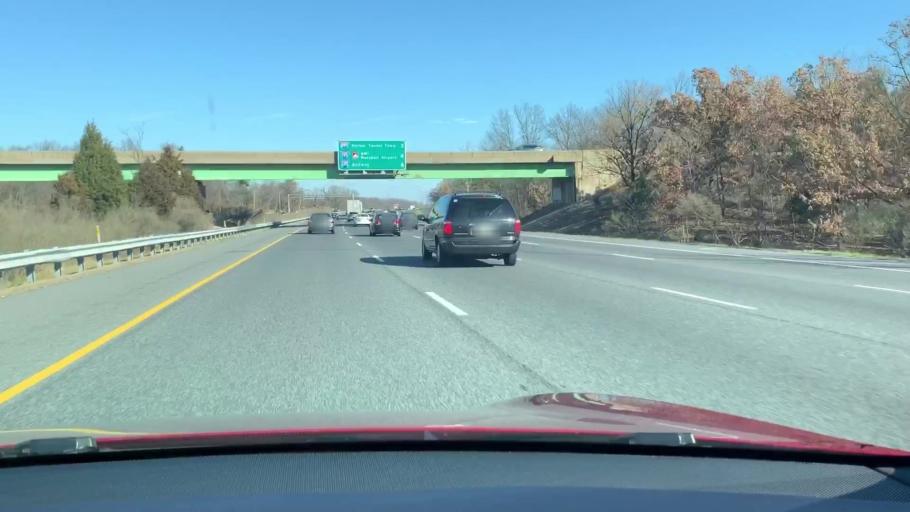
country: US
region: Maryland
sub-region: Howard County
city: West Elkridge
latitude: 39.1971
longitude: -76.7650
